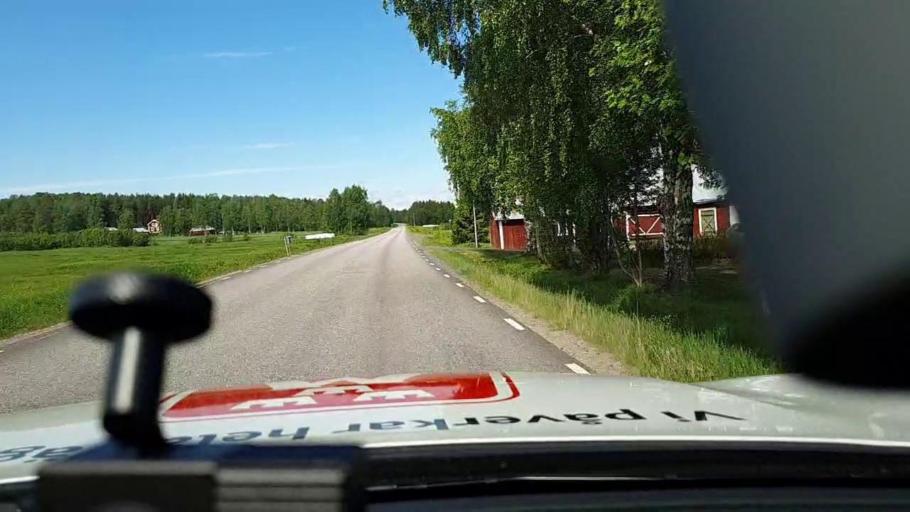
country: SE
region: Norrbotten
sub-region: Lulea Kommun
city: Sodra Sunderbyn
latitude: 65.6552
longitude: 21.8515
